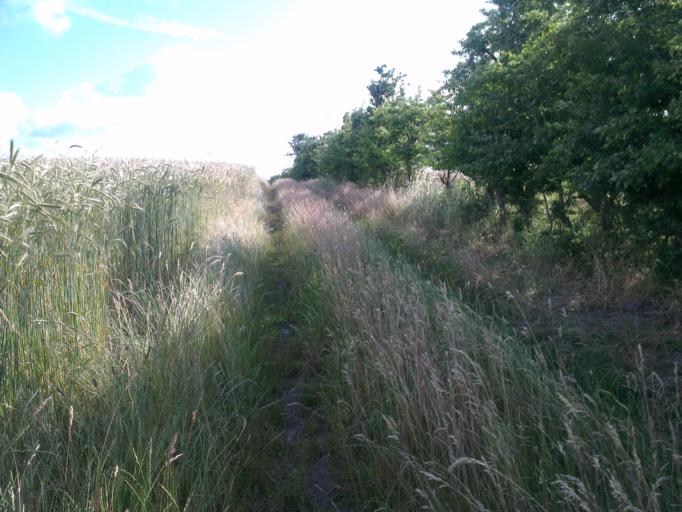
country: DK
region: Capital Region
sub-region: Frederikssund Kommune
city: Jaegerspris
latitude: 55.8751
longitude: 11.9774
